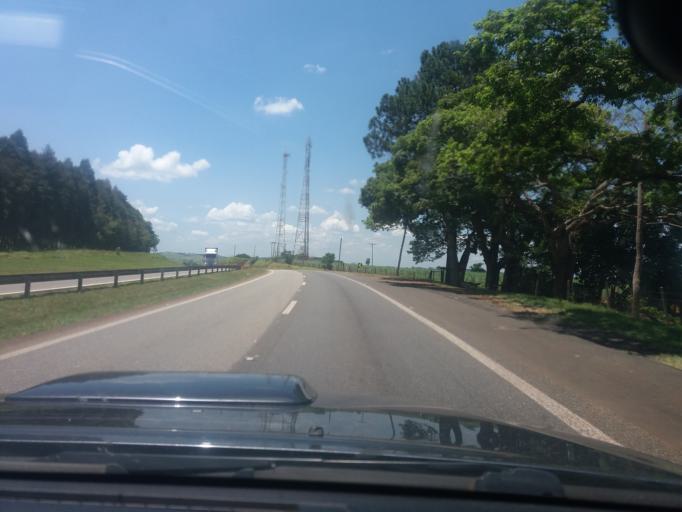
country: BR
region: Sao Paulo
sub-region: Tatui
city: Tatui
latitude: -23.3960
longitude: -47.9264
